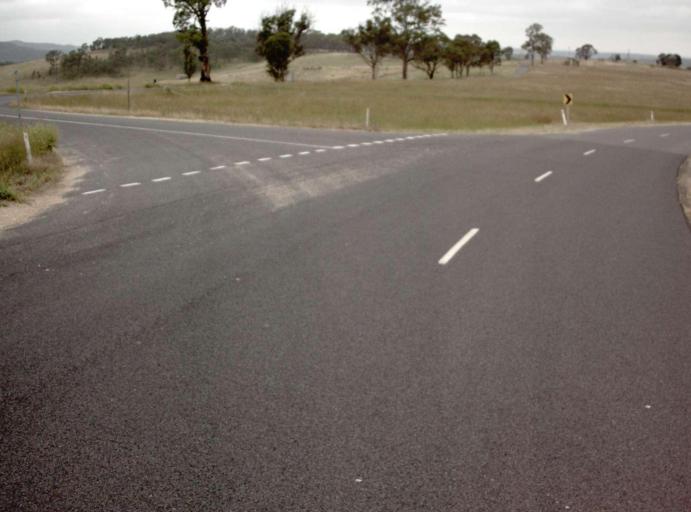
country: AU
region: Victoria
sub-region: Wellington
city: Heyfield
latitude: -37.8757
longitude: 146.7172
